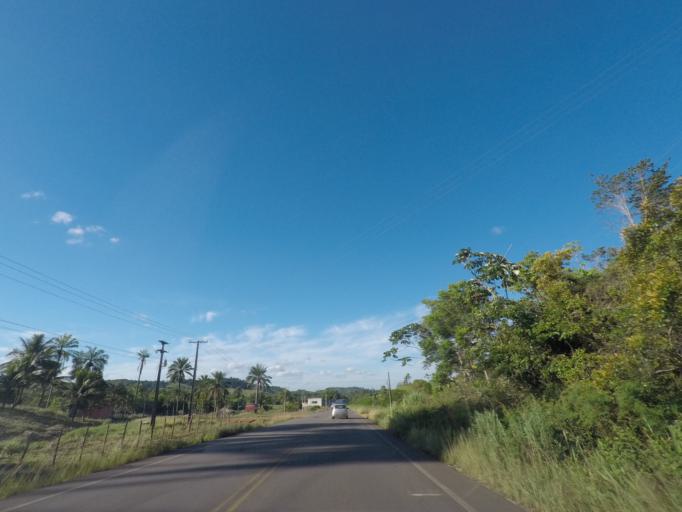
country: BR
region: Bahia
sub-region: Nazare
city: Nazare
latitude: -13.0672
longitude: -39.0040
